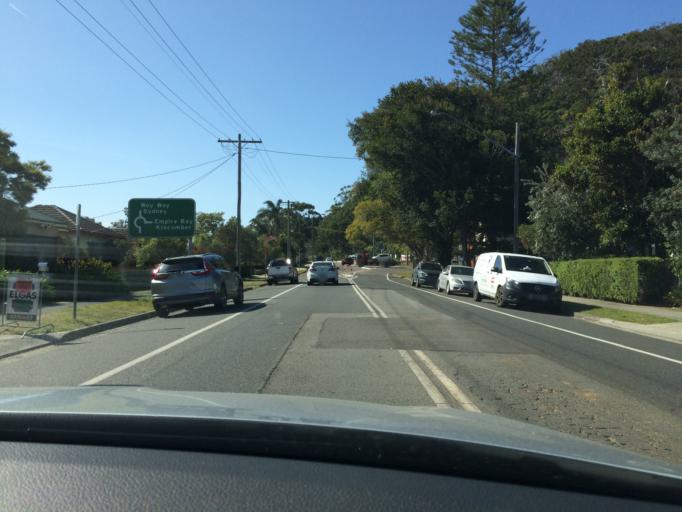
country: AU
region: New South Wales
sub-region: Gosford Shire
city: Ettalong Beach
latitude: -33.5106
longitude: 151.3307
